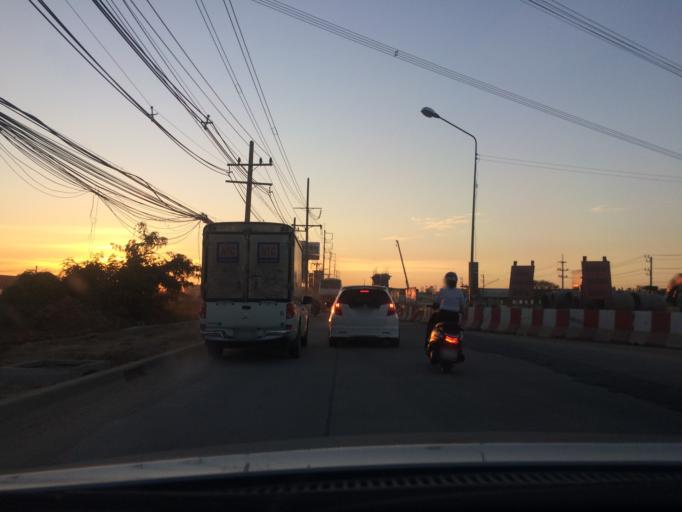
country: TH
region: Phitsanulok
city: Phitsanulok
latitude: 16.8181
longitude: 100.3362
